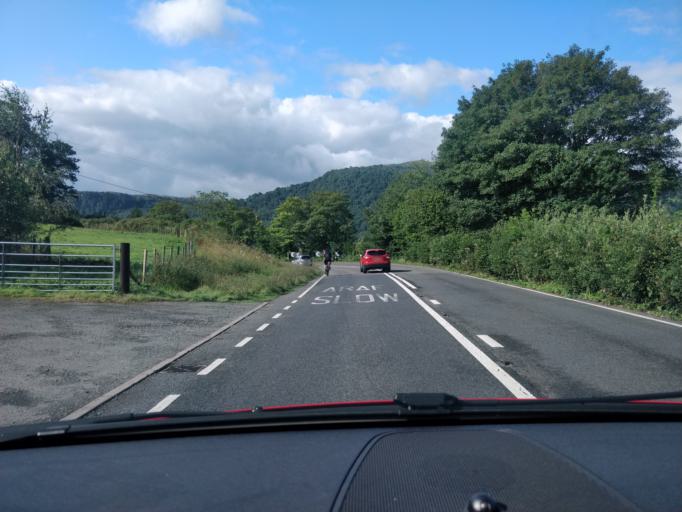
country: GB
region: Wales
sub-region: Conwy
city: Llanrwst
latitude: 53.1953
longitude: -3.8263
